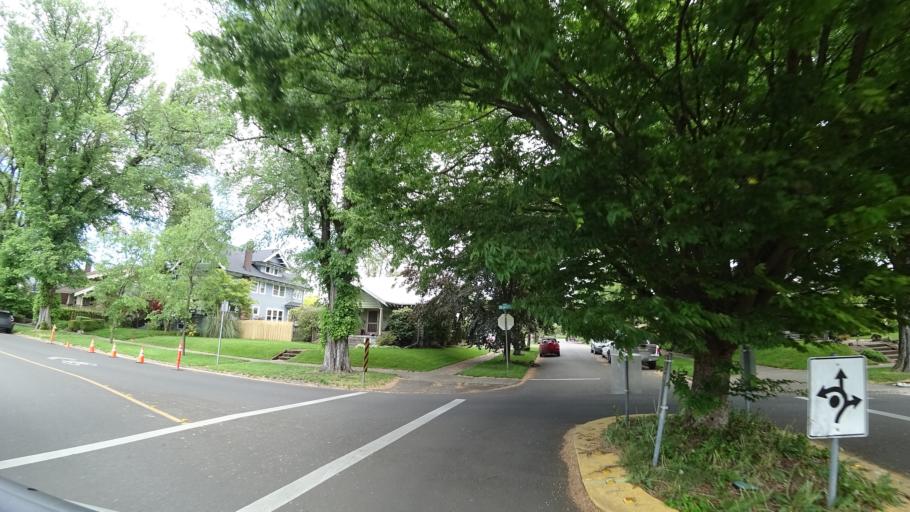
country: US
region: Oregon
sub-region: Multnomah County
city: Portland
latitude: 45.5069
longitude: -122.6474
